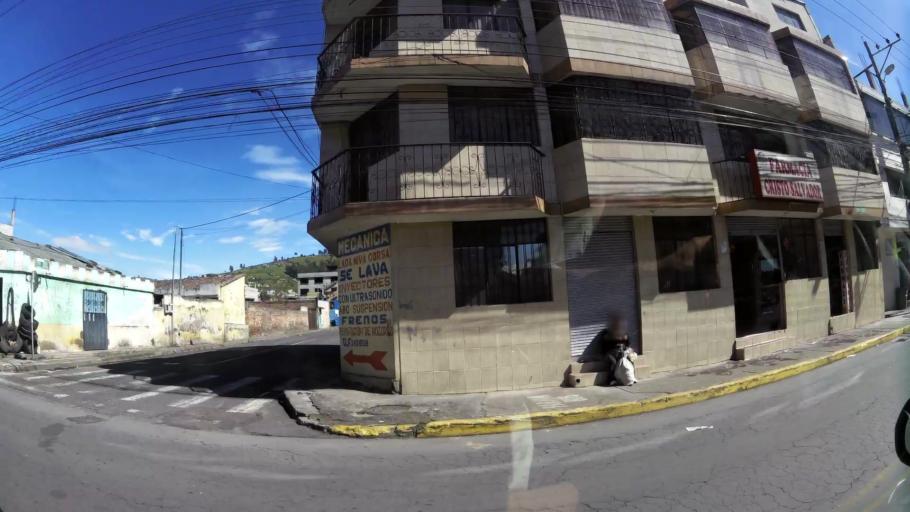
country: EC
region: Pichincha
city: Quito
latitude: -0.2835
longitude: -78.5588
